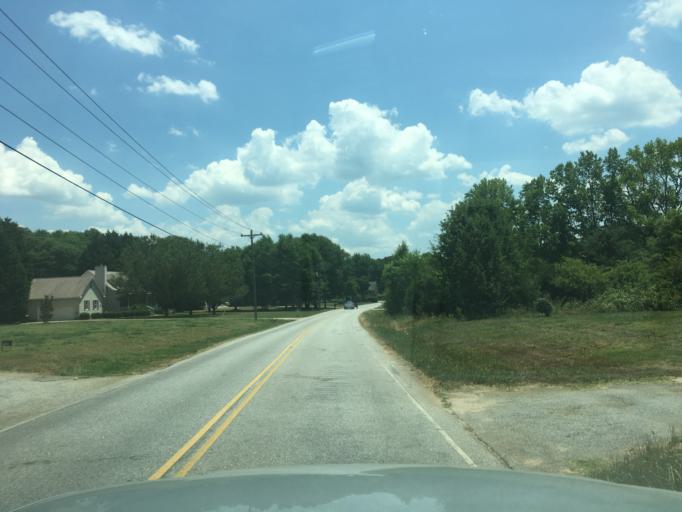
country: US
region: South Carolina
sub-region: Anderson County
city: Northlake
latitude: 34.5758
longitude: -82.6197
